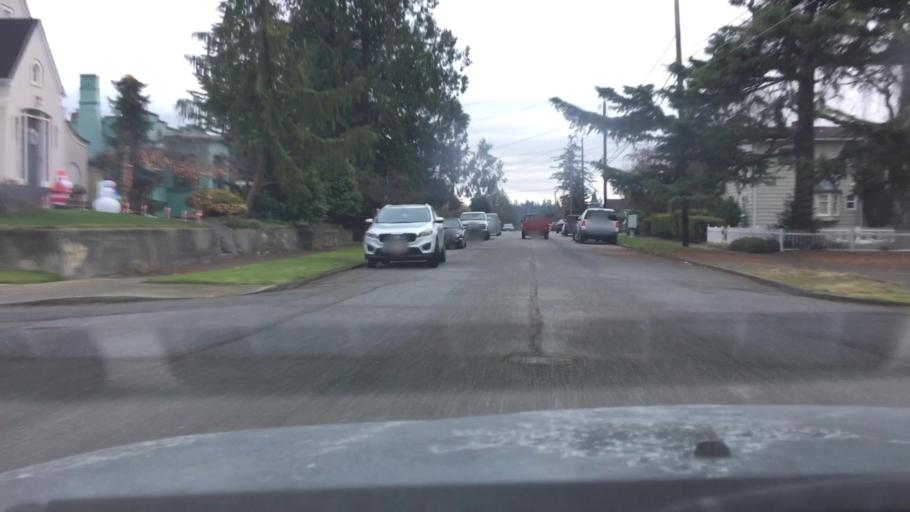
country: US
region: Washington
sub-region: Skagit County
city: Mount Vernon
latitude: 48.4202
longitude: -122.3287
